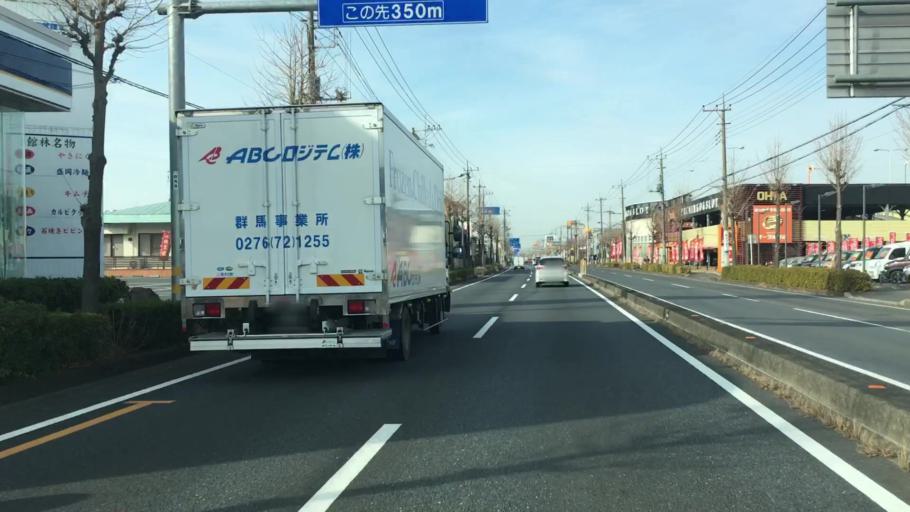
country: JP
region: Gunma
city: Tatebayashi
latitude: 36.2329
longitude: 139.5484
